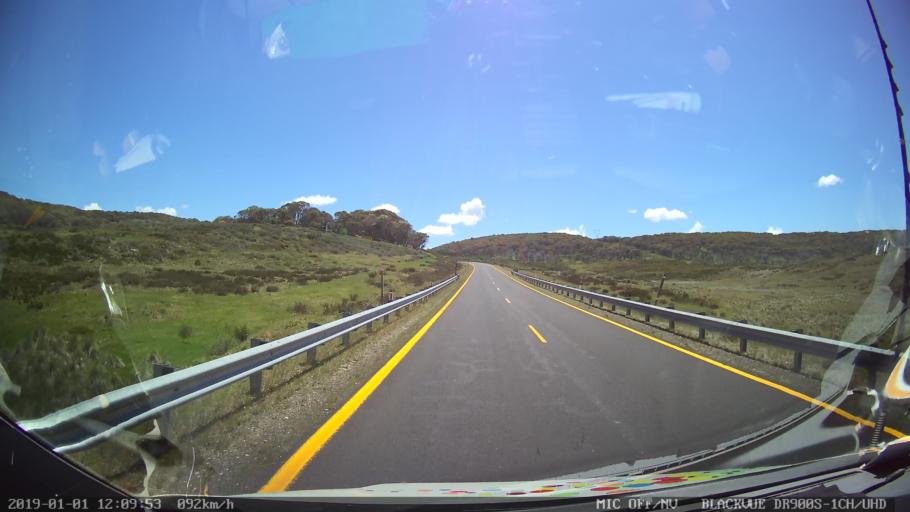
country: AU
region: New South Wales
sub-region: Tumut Shire
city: Tumut
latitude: -35.8019
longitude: 148.4972
